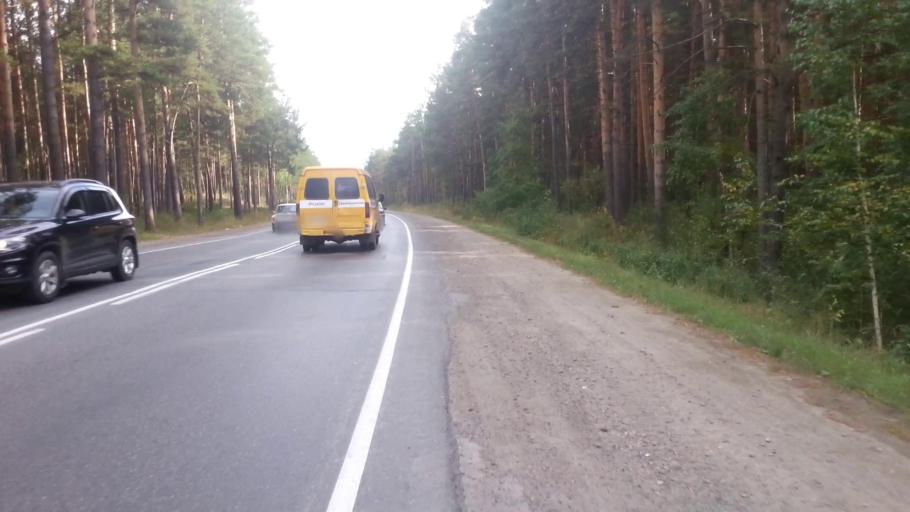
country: RU
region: Altai Krai
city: Yuzhnyy
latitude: 53.2980
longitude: 83.7030
